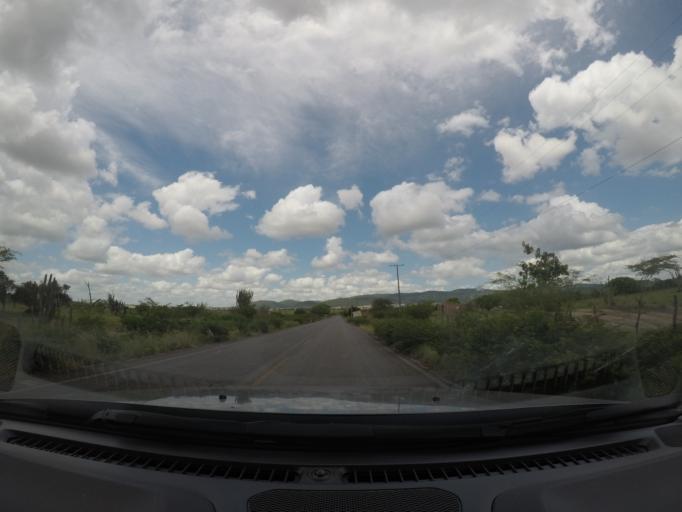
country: BR
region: Bahia
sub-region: Ipira
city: Ipira
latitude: -12.1747
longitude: -39.7559
